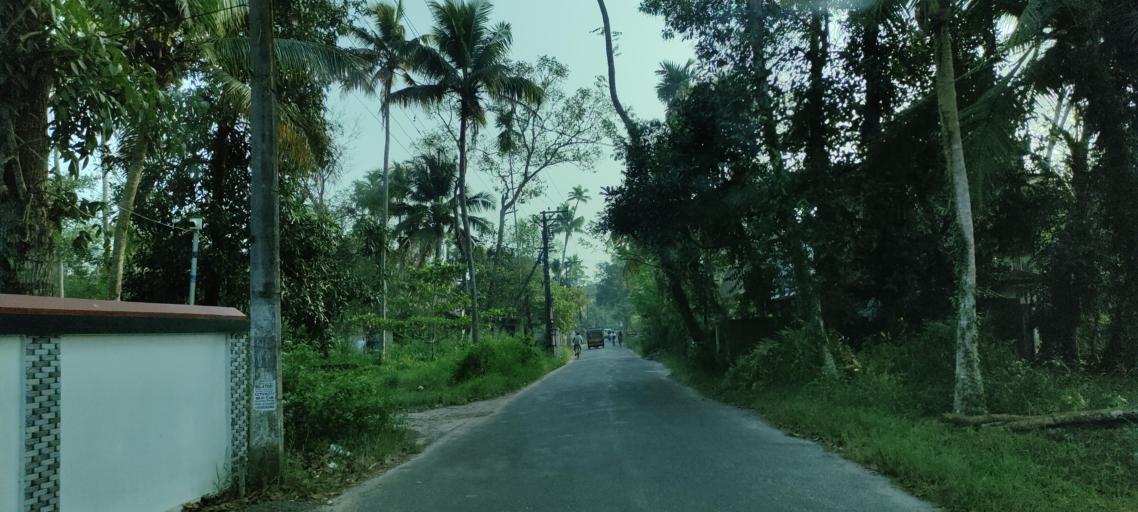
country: IN
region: Kerala
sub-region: Alappuzha
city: Shertallai
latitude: 9.6693
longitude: 76.3541
